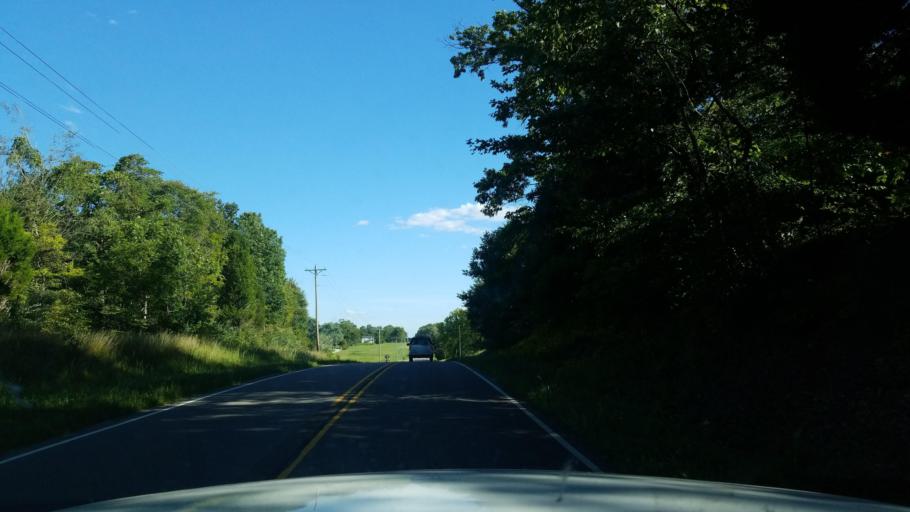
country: US
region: Illinois
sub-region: Saline County
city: Harrisburg
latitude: 37.6215
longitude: -88.4721
